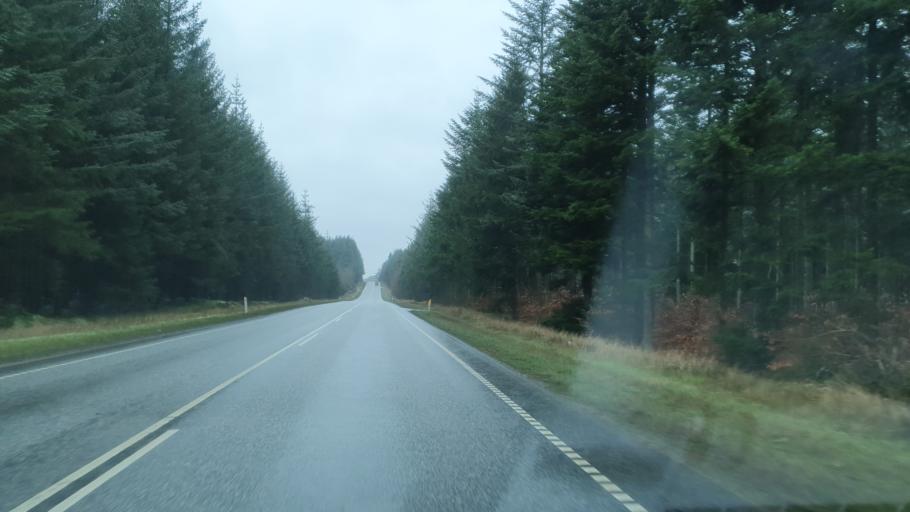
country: DK
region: North Denmark
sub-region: Jammerbugt Kommune
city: Fjerritslev
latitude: 57.0886
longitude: 9.3946
